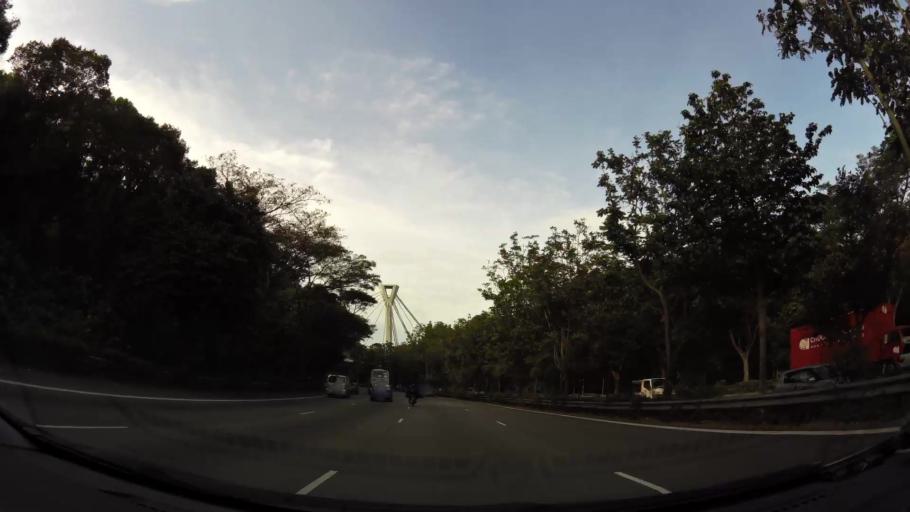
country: MY
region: Johor
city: Johor Bahru
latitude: 1.3391
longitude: 103.6786
